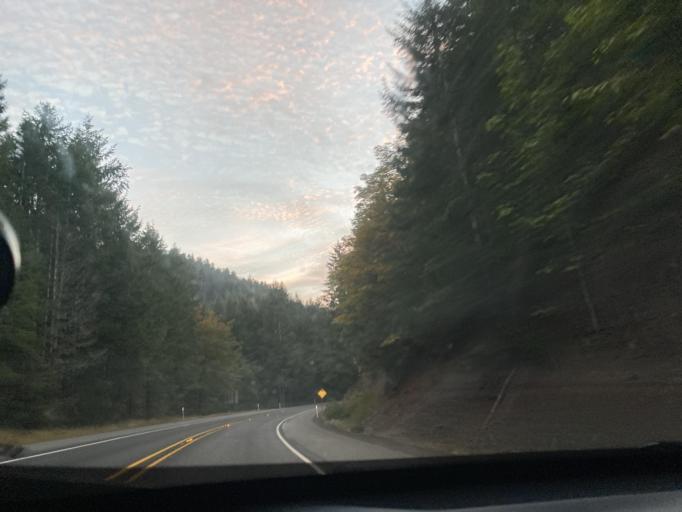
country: CA
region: British Columbia
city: Sooke
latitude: 48.0819
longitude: -123.7343
